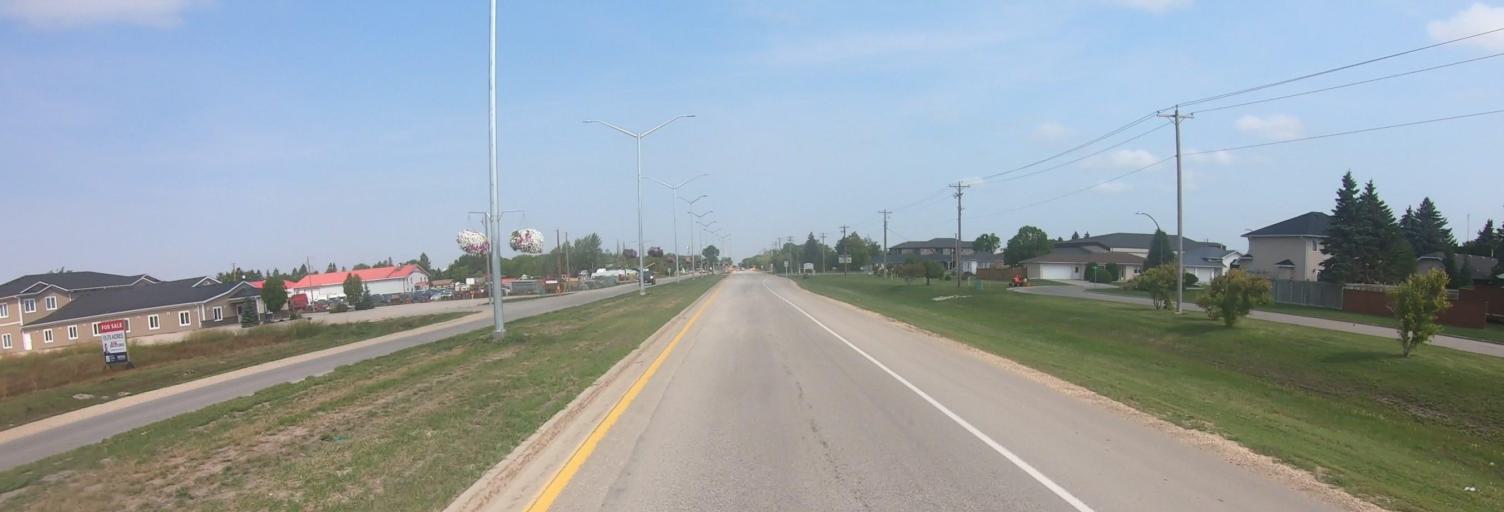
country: CA
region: Manitoba
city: Steinbach
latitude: 49.5116
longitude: -96.6916
